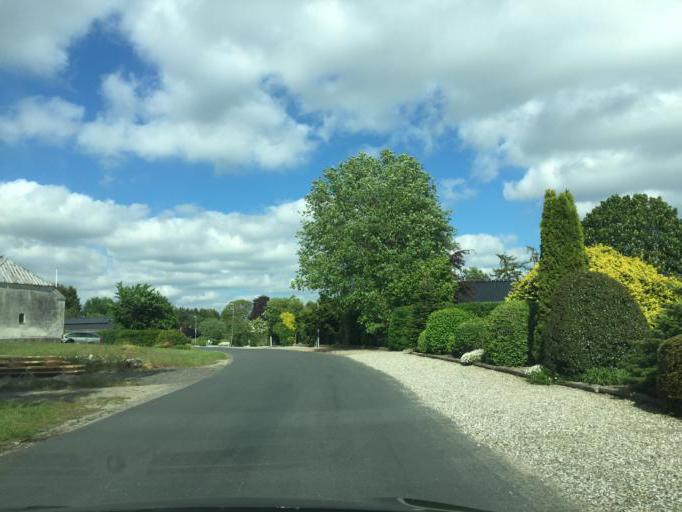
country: DK
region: South Denmark
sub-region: Odense Kommune
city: Bellinge
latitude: 55.3633
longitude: 10.2785
